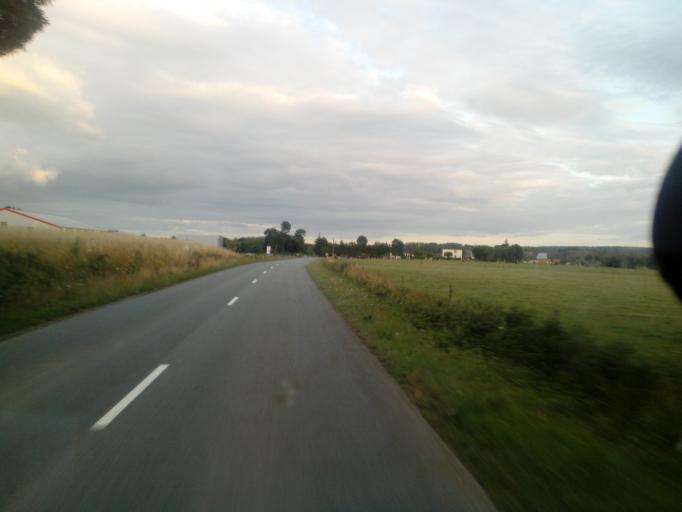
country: FR
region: Brittany
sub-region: Departement des Cotes-d'Armor
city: Plumieux
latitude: 48.0619
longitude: -2.5353
